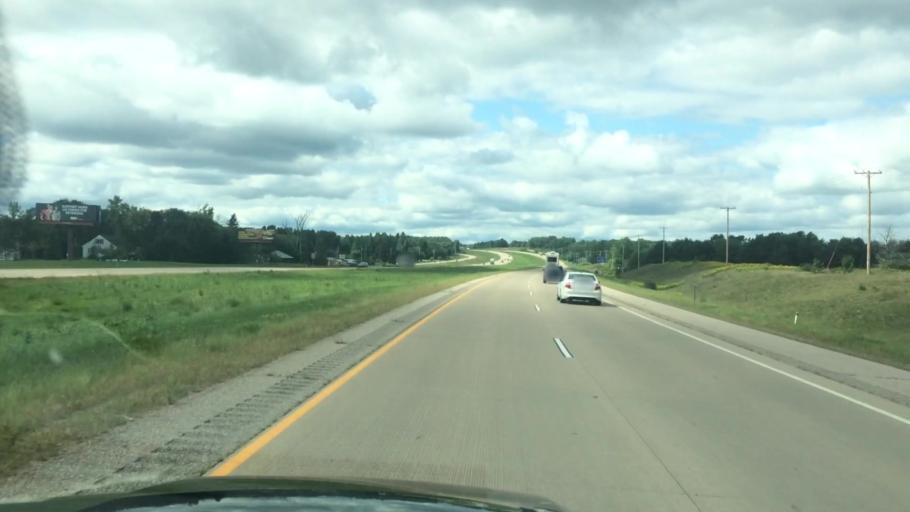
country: US
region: Wisconsin
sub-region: Portage County
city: Plover
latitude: 44.5096
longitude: -89.4211
